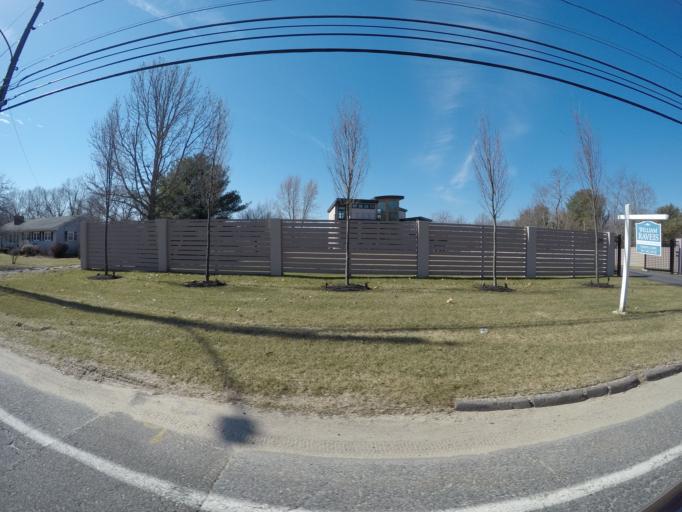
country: US
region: Massachusetts
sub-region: Norfolk County
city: Stoughton
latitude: 42.1079
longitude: -71.1323
